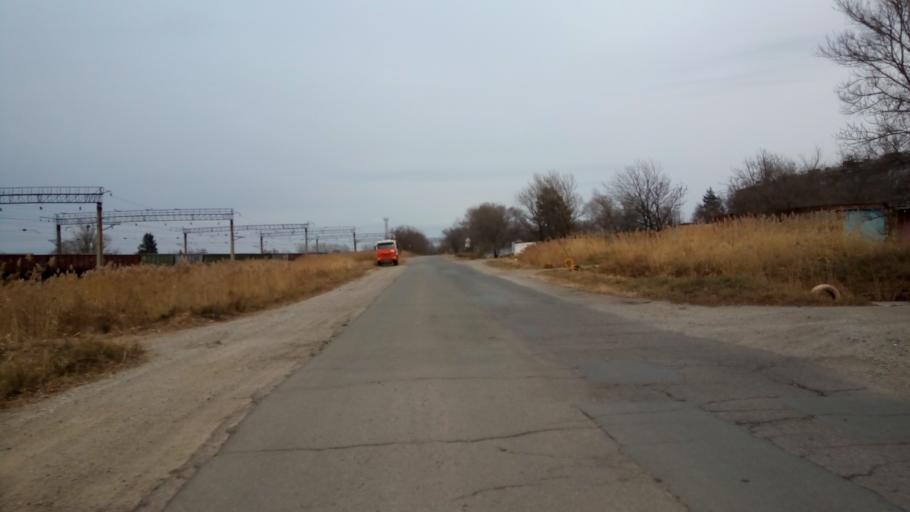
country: RU
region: Primorskiy
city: Novoshakhtinskiy
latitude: 44.0295
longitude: 132.1671
